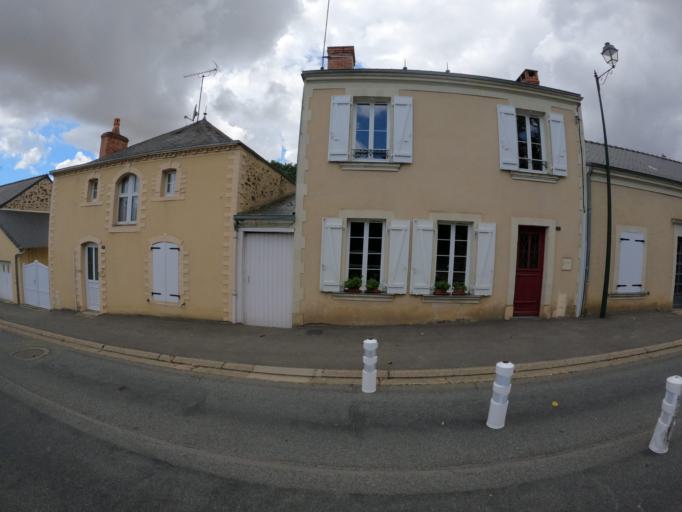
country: FR
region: Pays de la Loire
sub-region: Departement de Maine-et-Loire
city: Morannes
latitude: 47.7934
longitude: -0.4389
